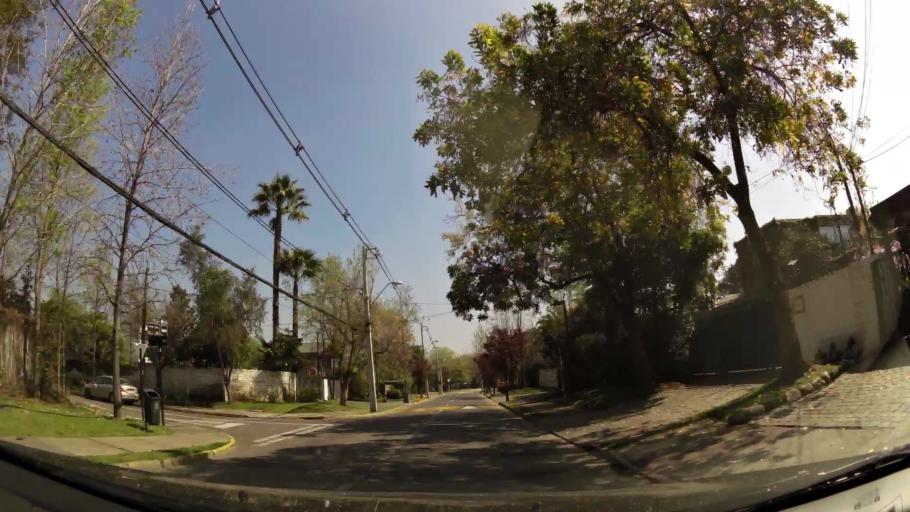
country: CL
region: Santiago Metropolitan
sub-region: Provincia de Santiago
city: Villa Presidente Frei, Nunoa, Santiago, Chile
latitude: -33.3855
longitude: -70.5821
